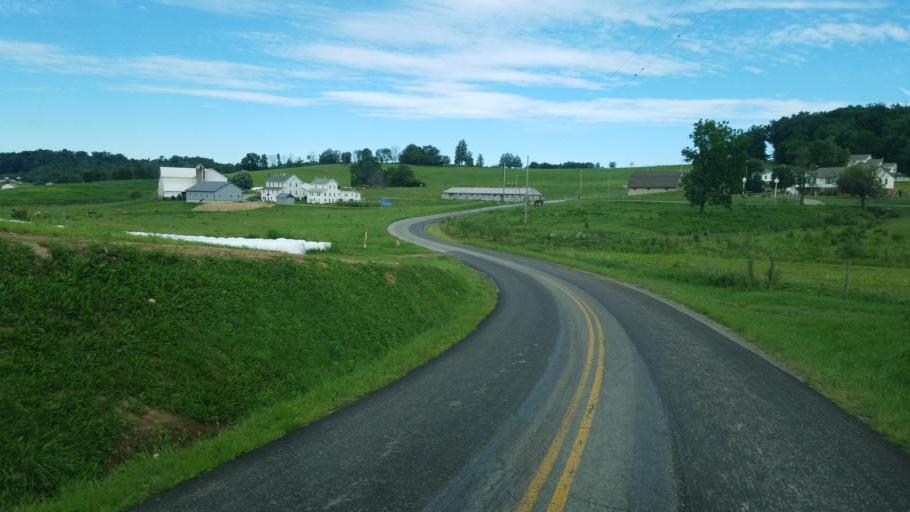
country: US
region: Ohio
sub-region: Holmes County
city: Millersburg
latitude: 40.5120
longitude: -81.8338
